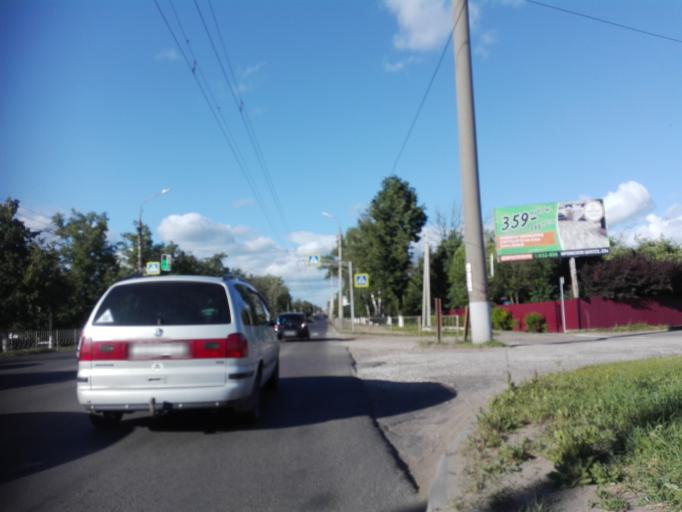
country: RU
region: Orjol
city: Orel
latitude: 52.9932
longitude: 36.1279
